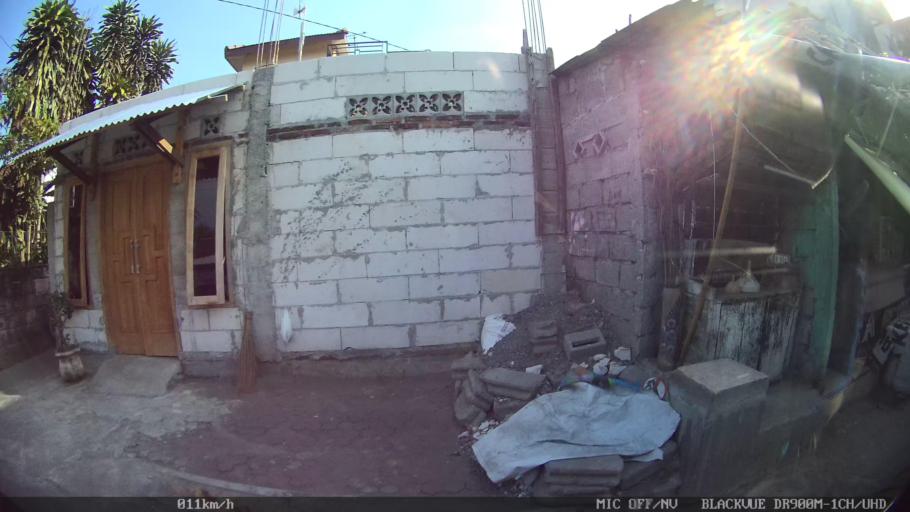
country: ID
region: Daerah Istimewa Yogyakarta
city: Yogyakarta
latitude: -7.7987
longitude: 110.3500
